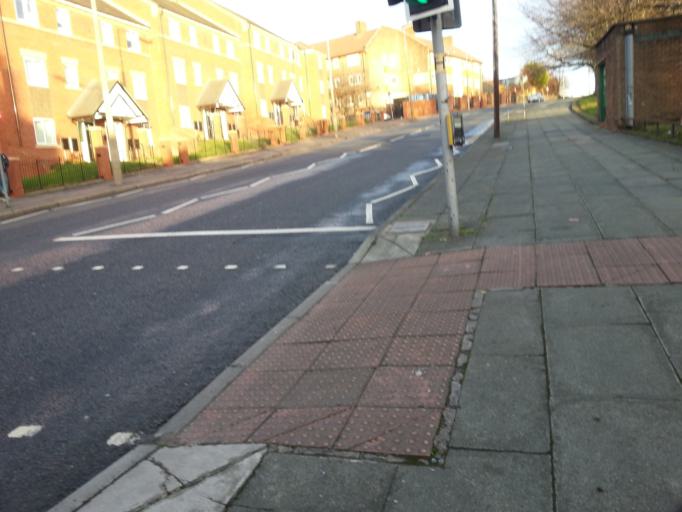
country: GB
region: England
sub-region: Liverpool
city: Liverpool
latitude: 53.4034
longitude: -2.9584
